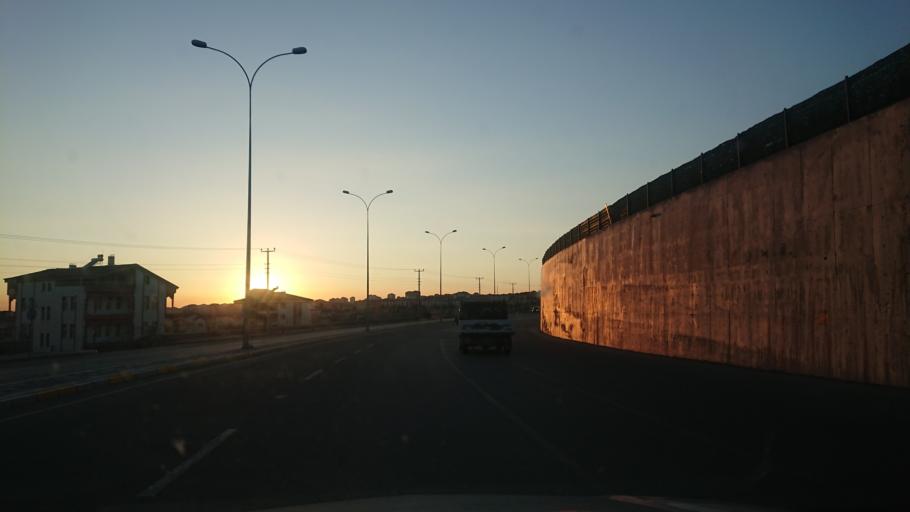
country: TR
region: Aksaray
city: Aksaray
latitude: 38.4035
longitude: 34.0145
